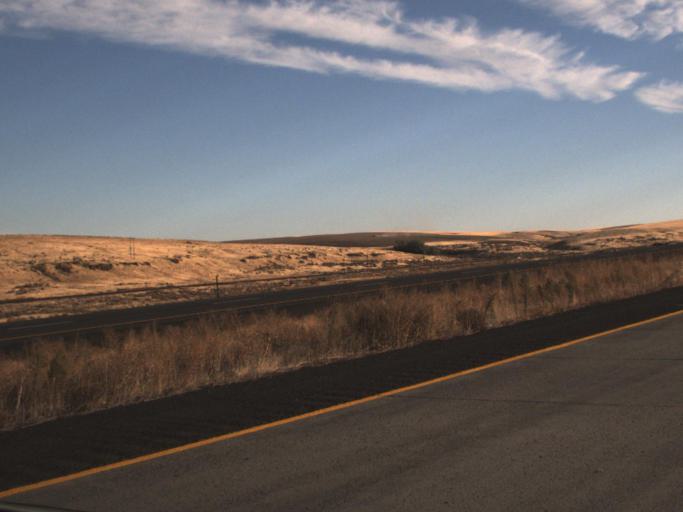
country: US
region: Washington
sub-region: Adams County
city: Ritzville
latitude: 47.0003
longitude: -118.5369
